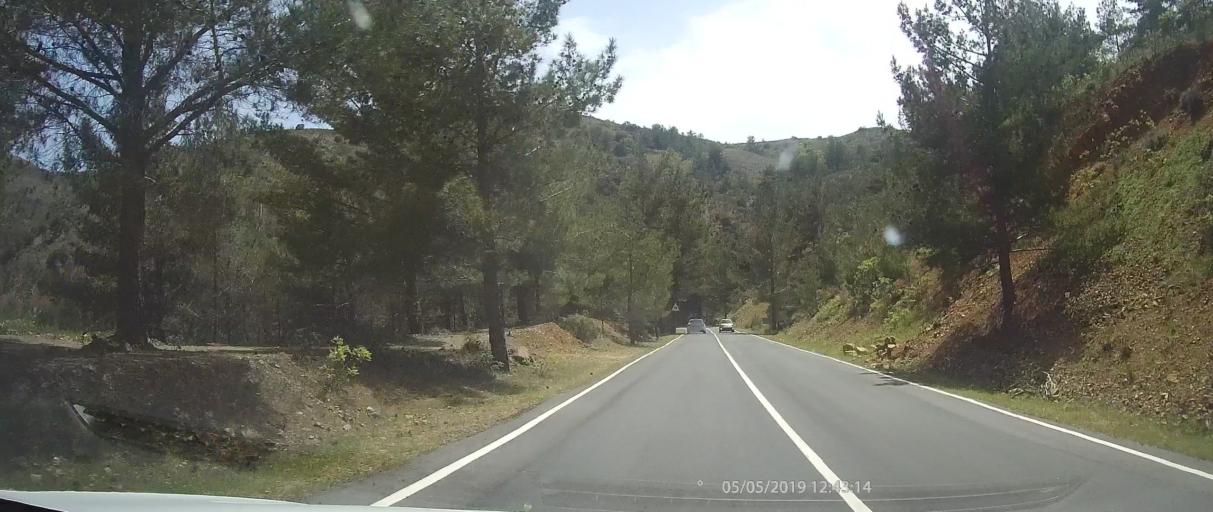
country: CY
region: Lefkosia
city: Kakopetria
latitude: 34.9695
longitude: 32.8135
